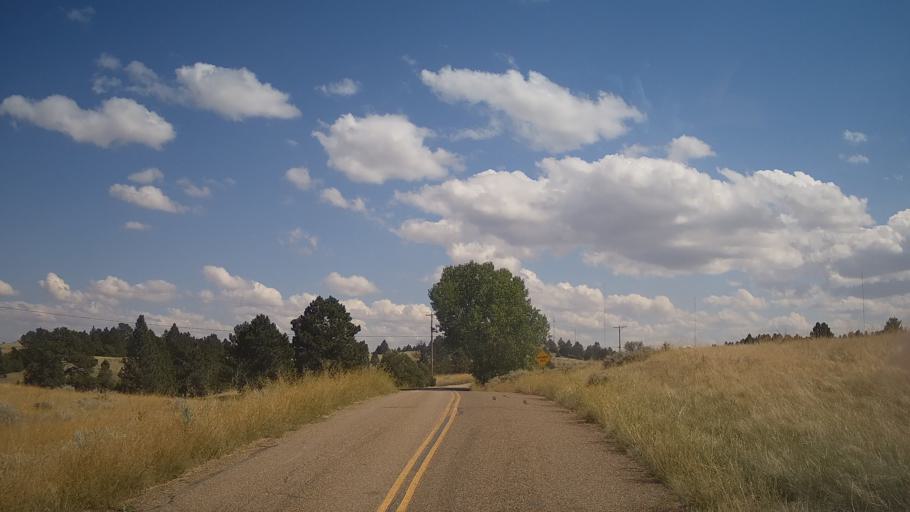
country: US
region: Montana
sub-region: Dawson County
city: Glendive
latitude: 47.0610
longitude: -104.6816
